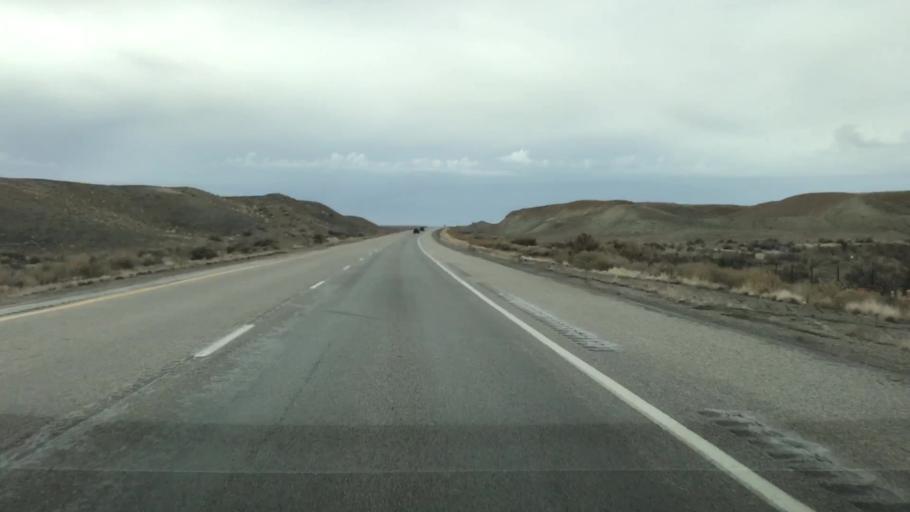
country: US
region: Utah
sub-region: Grand County
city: Moab
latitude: 38.9763
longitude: -109.3538
